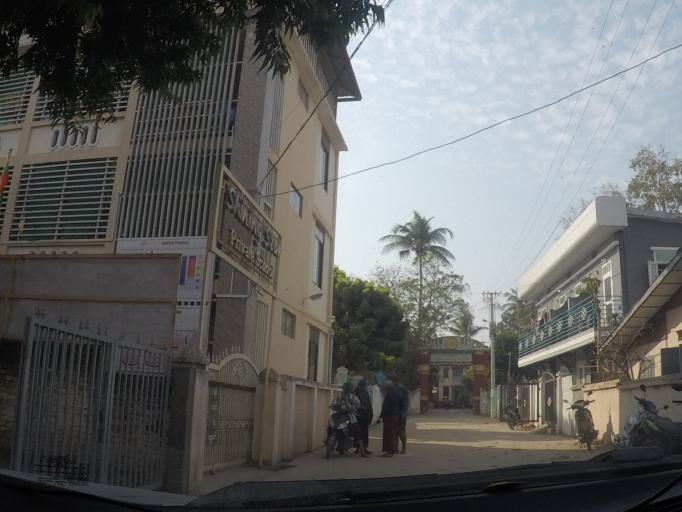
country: MM
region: Bago
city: Pyay
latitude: 18.8196
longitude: 95.2440
